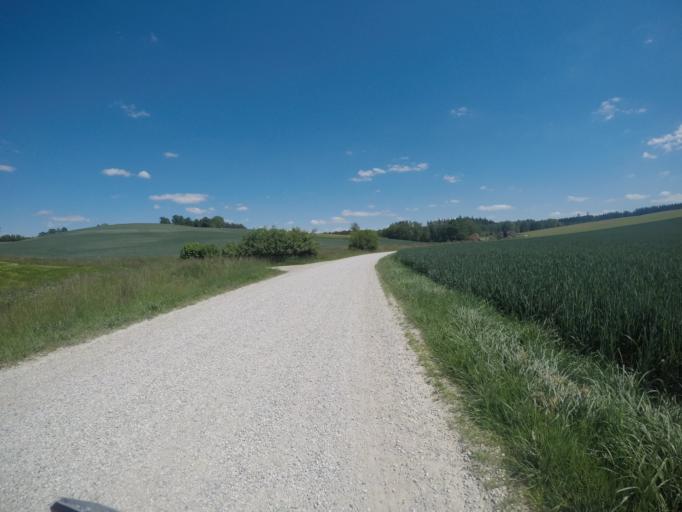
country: DE
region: Bavaria
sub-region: Lower Bavaria
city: Kumhausen
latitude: 48.4864
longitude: 12.1663
